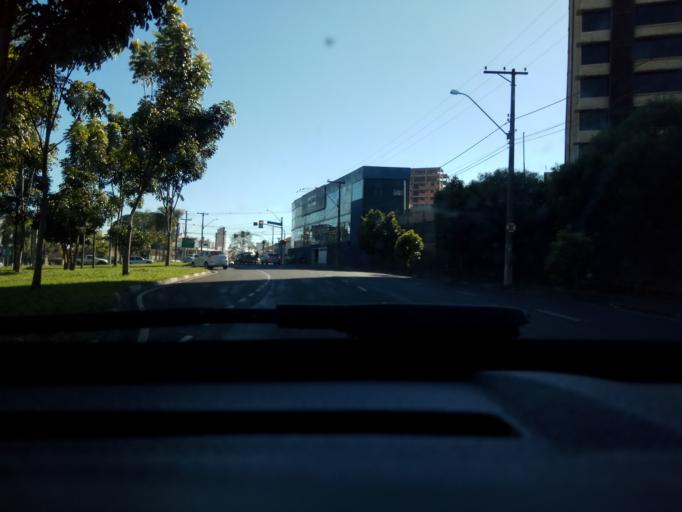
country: BR
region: Sao Paulo
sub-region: Piracicaba
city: Piracicaba
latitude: -22.7366
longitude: -47.6477
